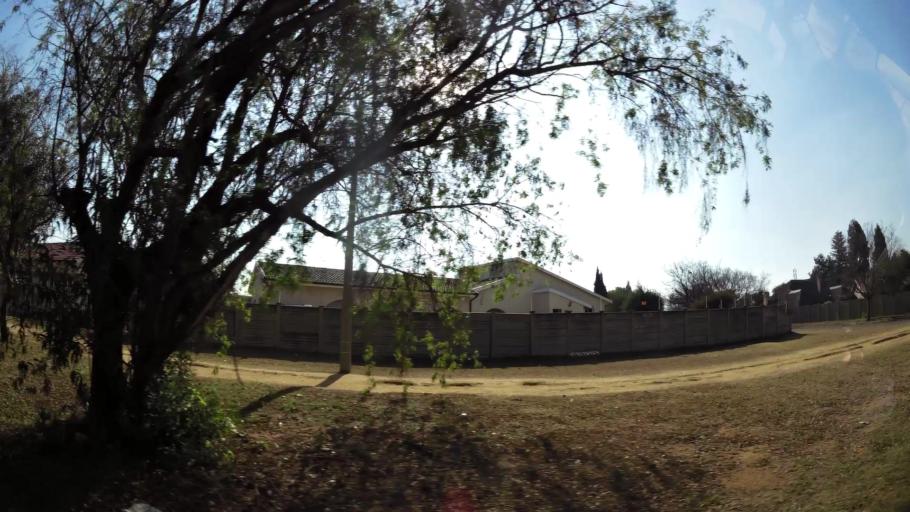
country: ZA
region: Gauteng
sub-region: West Rand District Municipality
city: Randfontein
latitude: -26.1858
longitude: 27.6821
